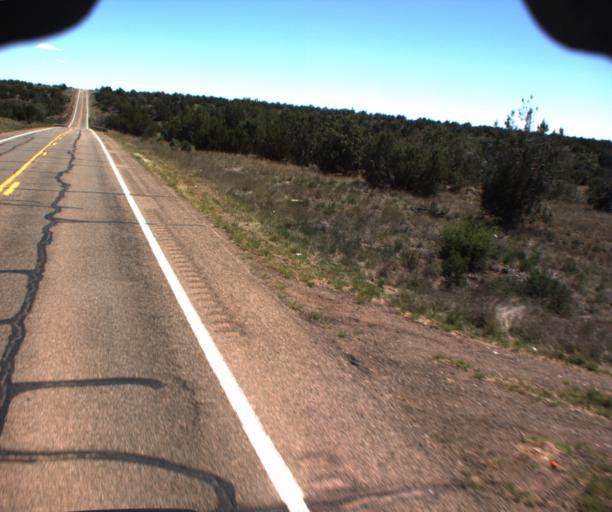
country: US
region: Arizona
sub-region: Coconino County
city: Williams
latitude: 35.2018
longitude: -112.4743
